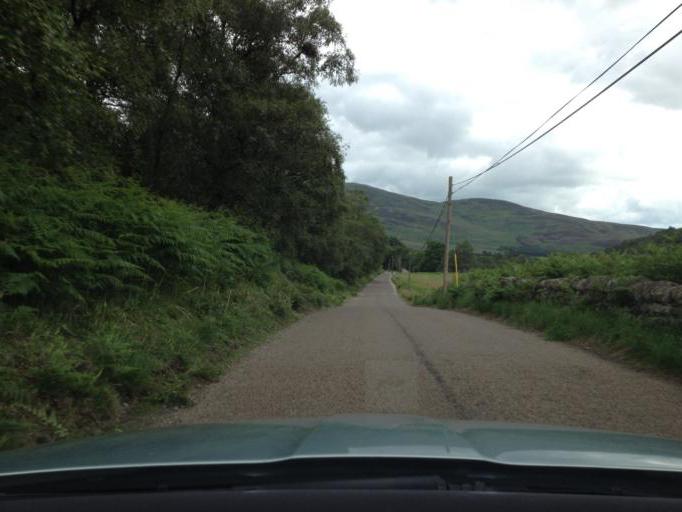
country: GB
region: Scotland
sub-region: Angus
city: Brechin
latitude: 56.8952
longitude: -2.7362
